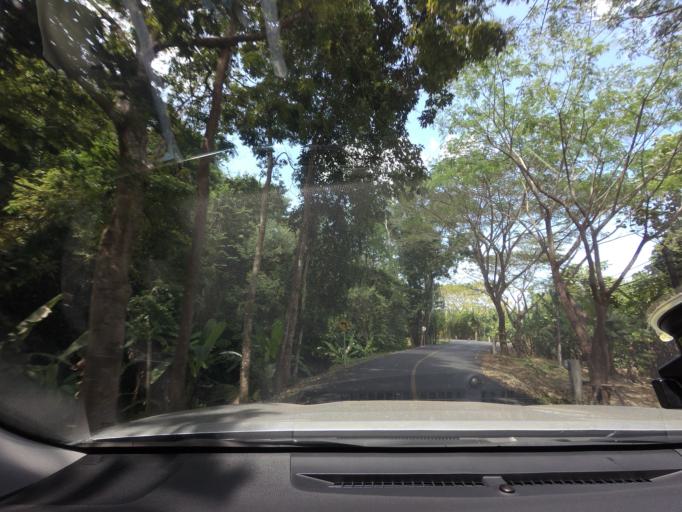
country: TH
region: Phuket
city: Mueang Phuket
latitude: 7.8740
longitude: 98.3528
